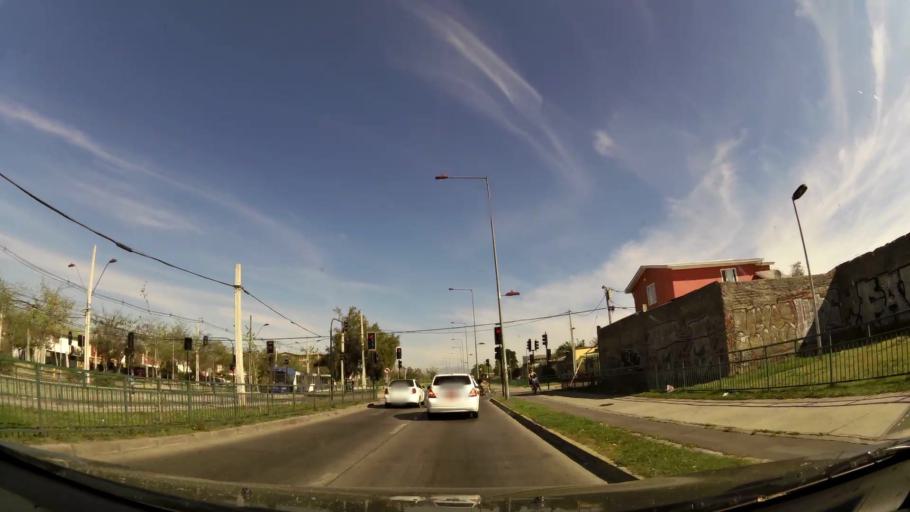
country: CL
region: Santiago Metropolitan
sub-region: Provincia de Santiago
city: Santiago
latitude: -33.4872
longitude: -70.6299
